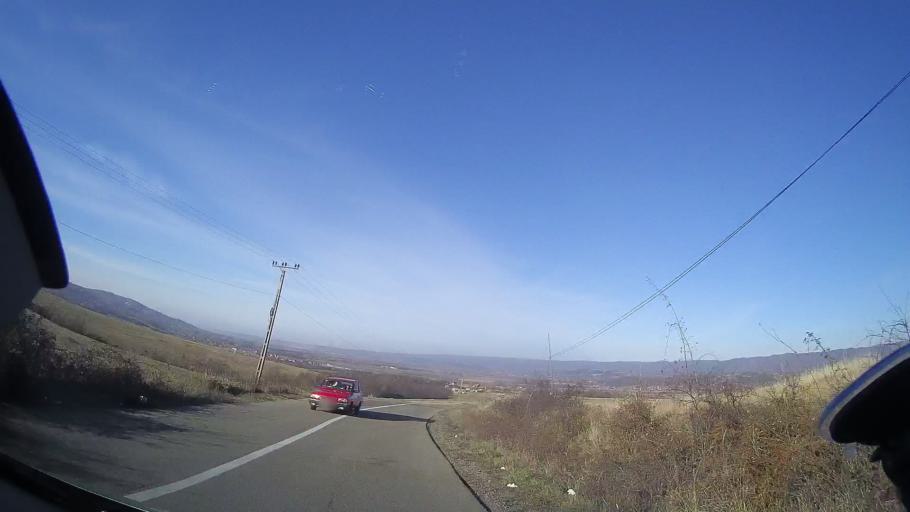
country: RO
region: Bihor
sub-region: Comuna Vadu Crisului
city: Vadu Crisului
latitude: 46.9779
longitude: 22.5339
